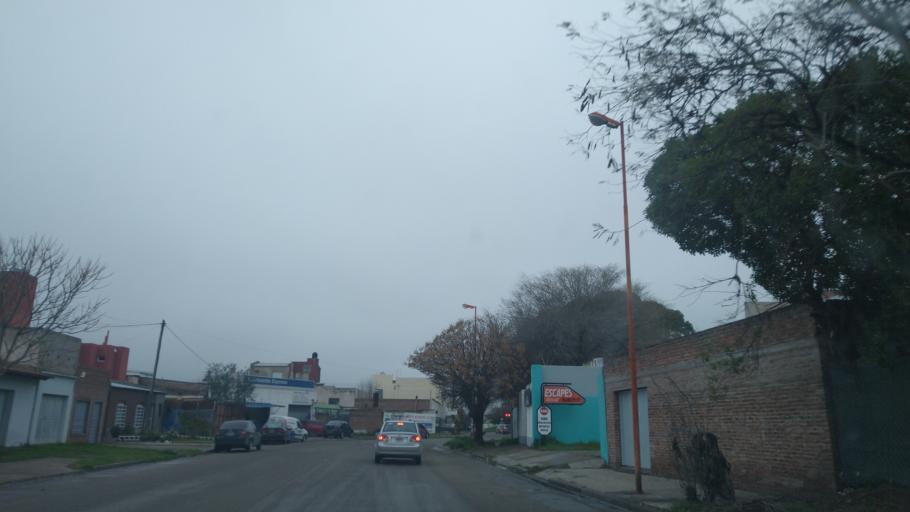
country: AR
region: Buenos Aires
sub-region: Partido de Bahia Blanca
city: Bahia Blanca
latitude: -38.7428
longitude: -62.2362
